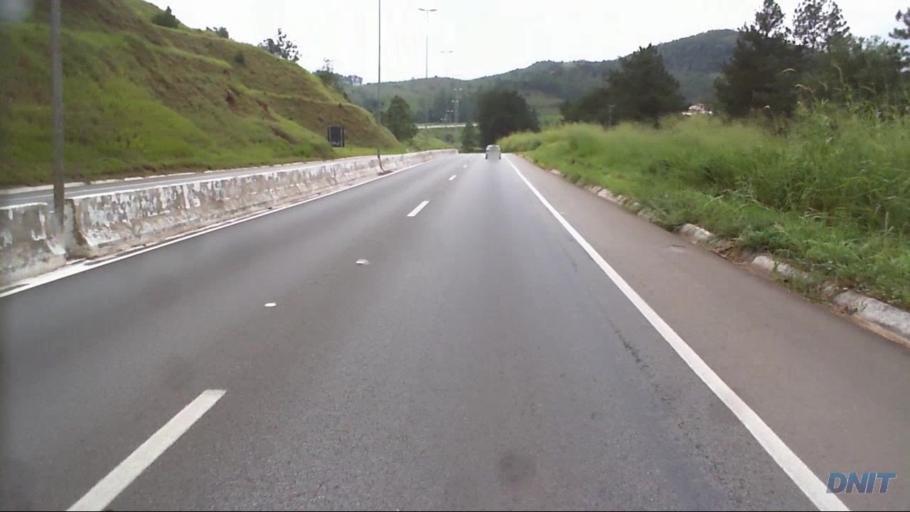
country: BR
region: Minas Gerais
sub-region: Nova Era
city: Nova Era
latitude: -19.7695
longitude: -43.0470
